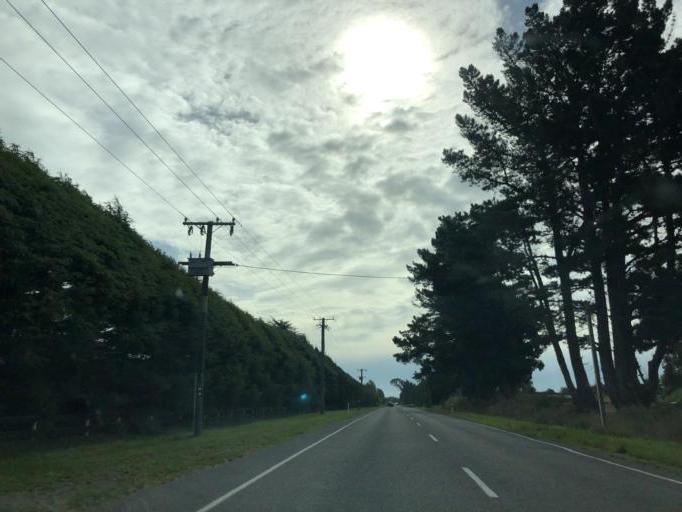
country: NZ
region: Canterbury
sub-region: Selwyn District
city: Rolleston
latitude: -43.6255
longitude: 172.4150
